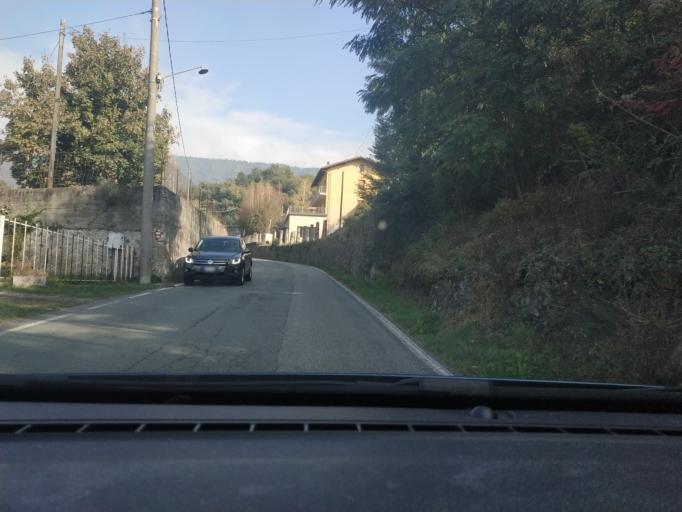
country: IT
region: Piedmont
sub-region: Provincia di Torino
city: Chiaverano
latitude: 45.4932
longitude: 7.9029
